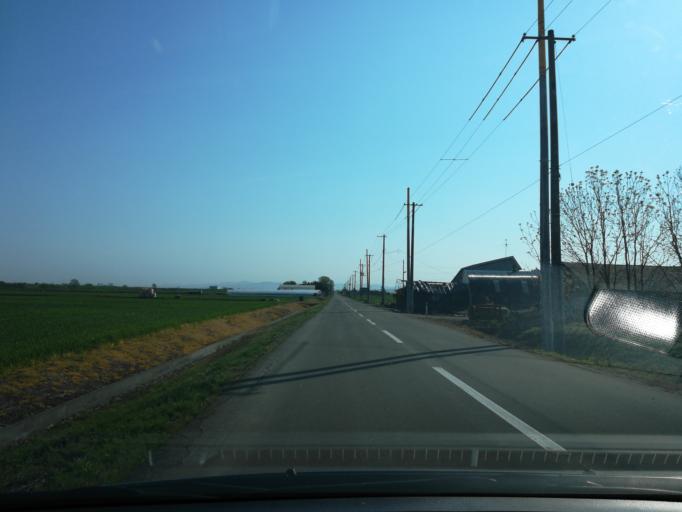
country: JP
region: Hokkaido
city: Iwamizawa
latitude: 43.1267
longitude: 141.6679
